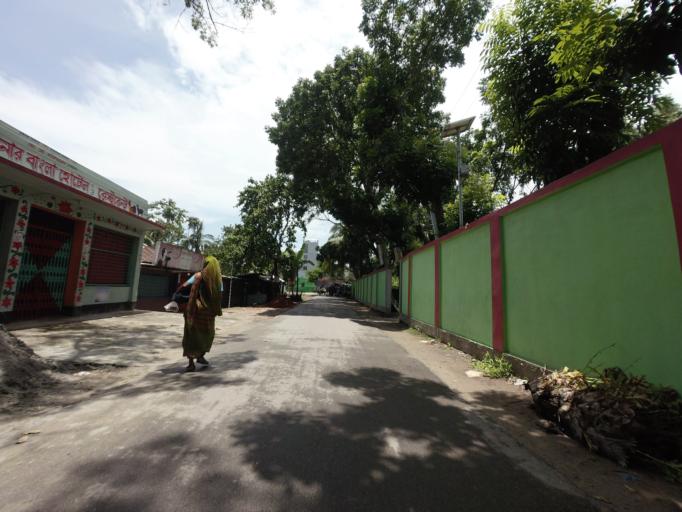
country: BD
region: Khulna
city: Kalia
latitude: 23.0409
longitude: 89.6335
